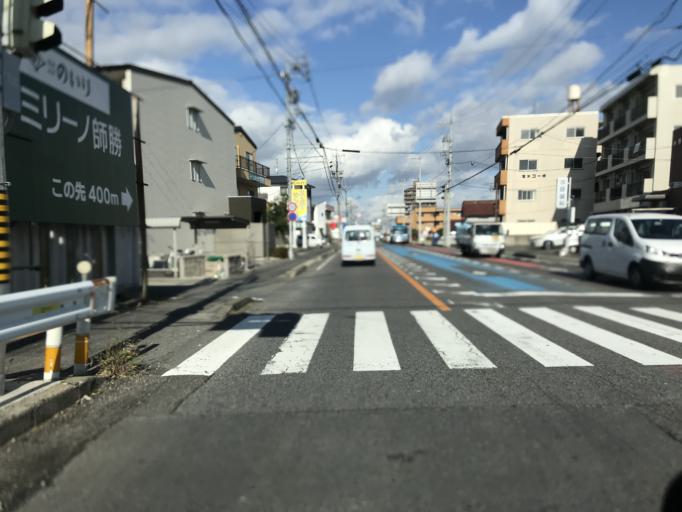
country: JP
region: Aichi
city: Komaki
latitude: 35.2435
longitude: 136.8955
